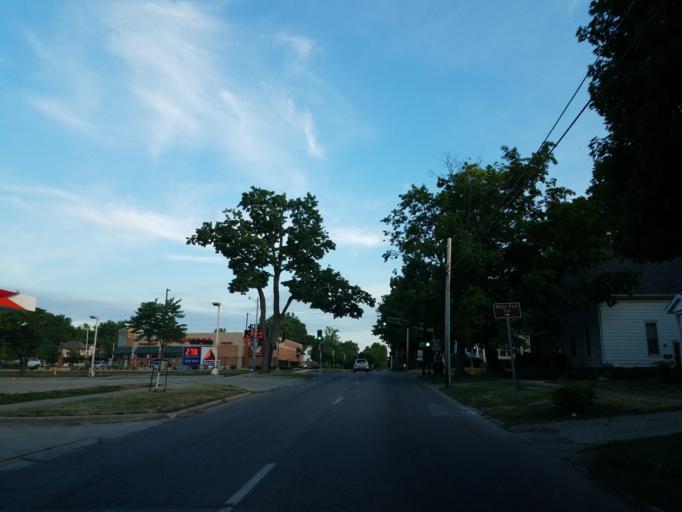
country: US
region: Illinois
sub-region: McLean County
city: Bloomington
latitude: 40.4719
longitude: -88.9943
